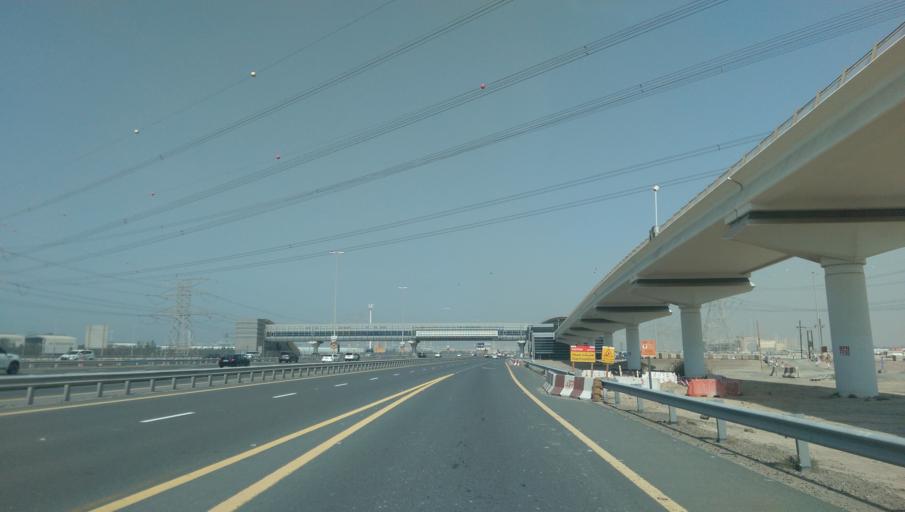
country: AE
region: Dubai
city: Dubai
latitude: 25.0237
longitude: 55.1000
